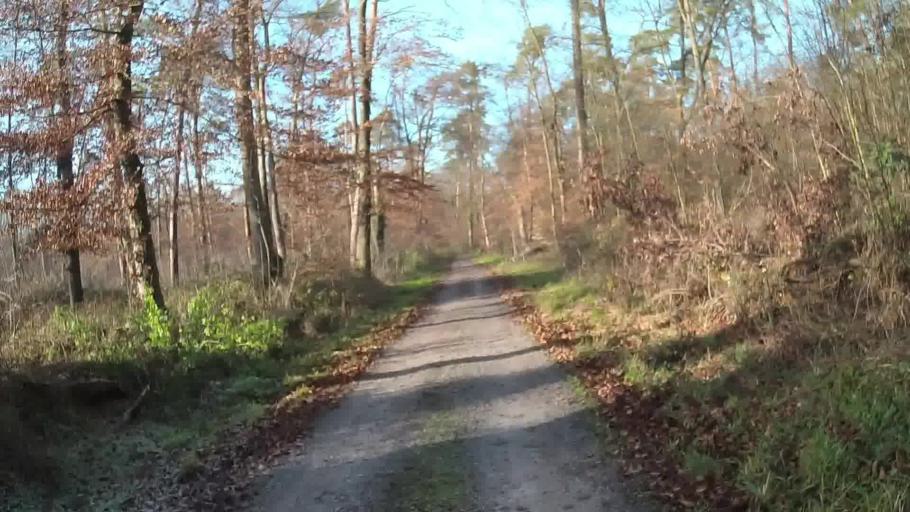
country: DE
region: Baden-Wuerttemberg
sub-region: Karlsruhe Region
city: Walldorf
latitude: 49.2740
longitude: 8.6539
